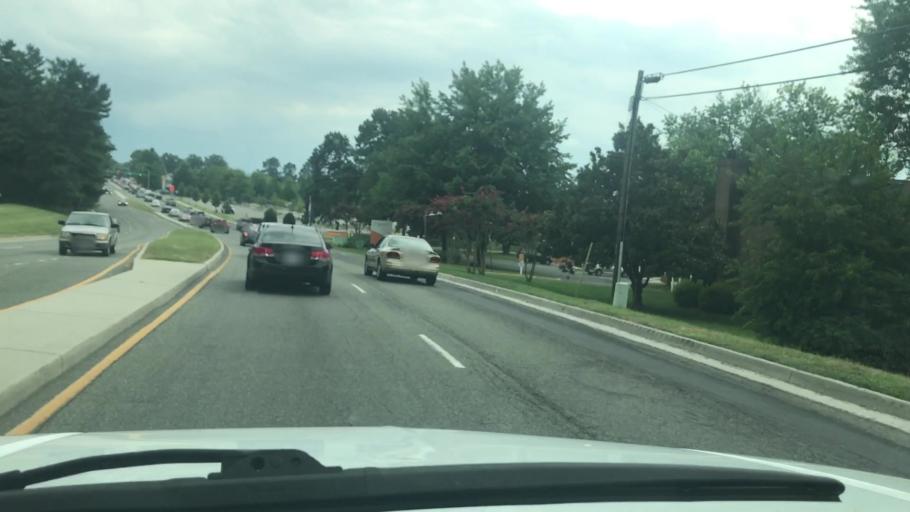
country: US
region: Virginia
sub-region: Henrico County
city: Tuckahoe
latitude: 37.6069
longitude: -77.5648
